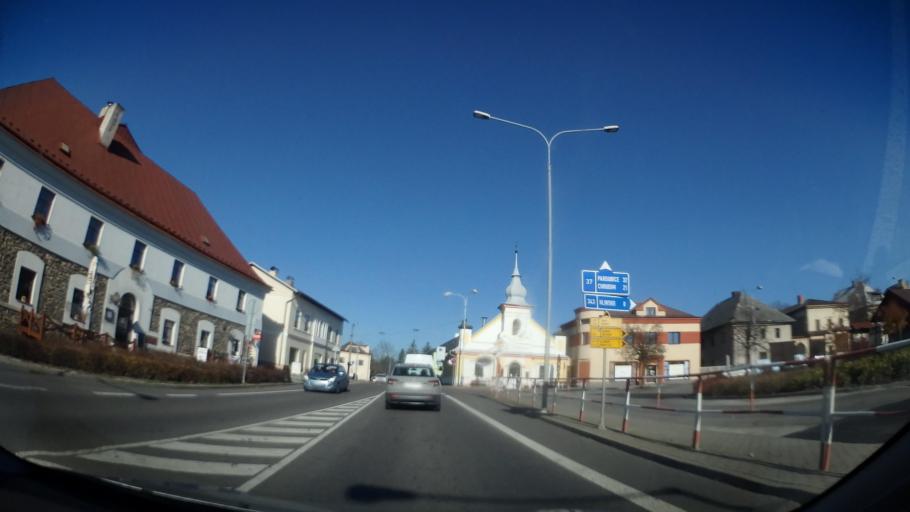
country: CZ
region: Pardubicky
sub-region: Okres Chrudim
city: Nasavrky
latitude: 49.7863
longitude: 15.8161
